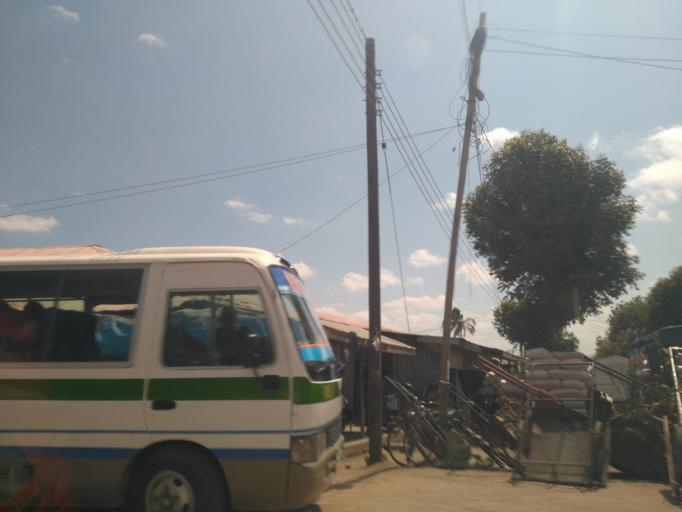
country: TZ
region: Dodoma
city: Dodoma
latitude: -6.1768
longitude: 35.7404
